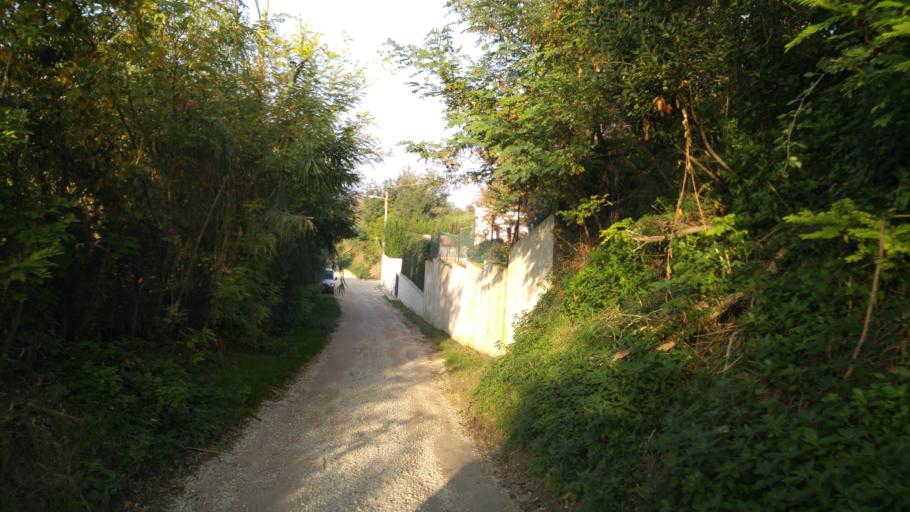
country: IT
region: The Marches
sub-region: Provincia di Pesaro e Urbino
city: Fenile
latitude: 43.8777
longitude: 12.9628
